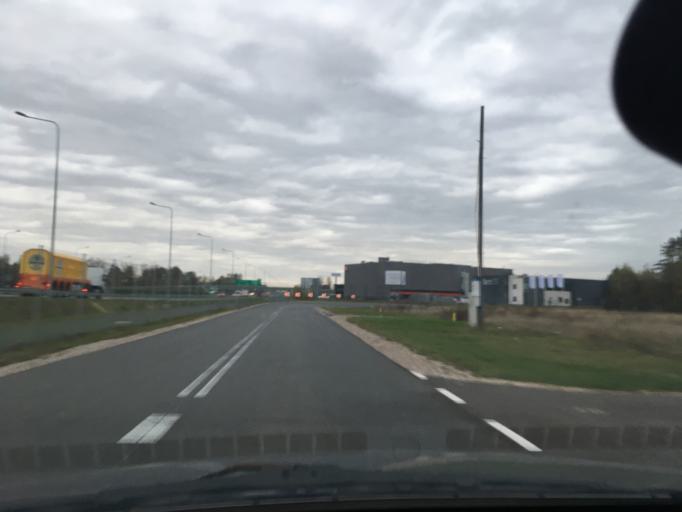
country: PL
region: Lodz Voivodeship
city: Zabia Wola
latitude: 52.0489
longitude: 20.7138
